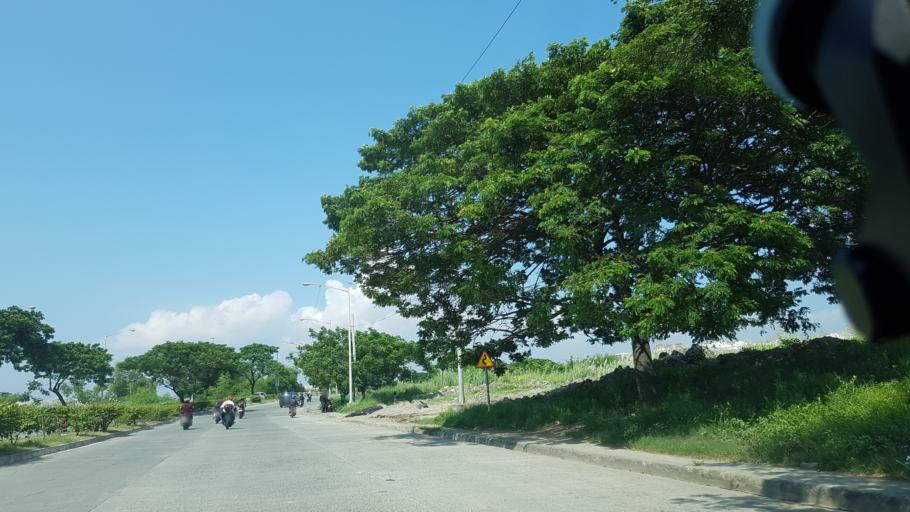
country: PH
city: Sambayanihan People's Village
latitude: 14.4819
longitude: 120.9881
